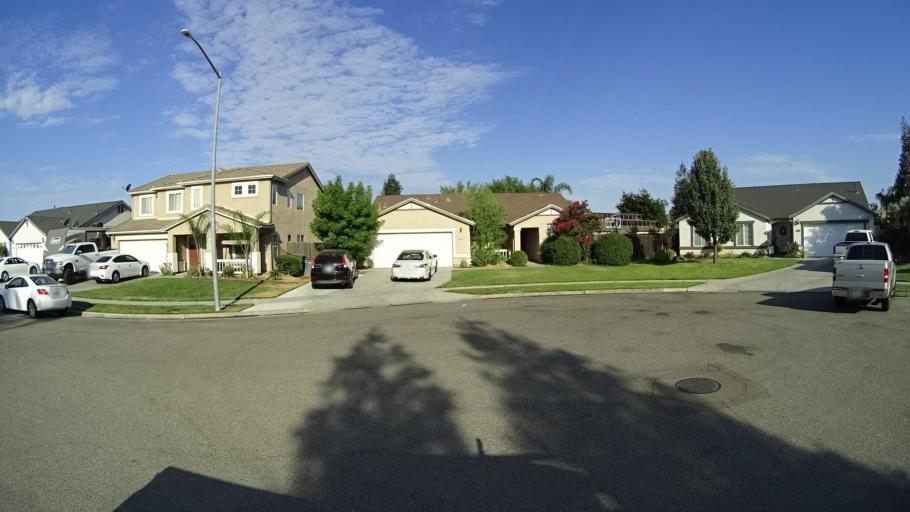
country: US
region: California
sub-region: Fresno County
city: Tarpey Village
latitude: 36.7918
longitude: -119.6751
